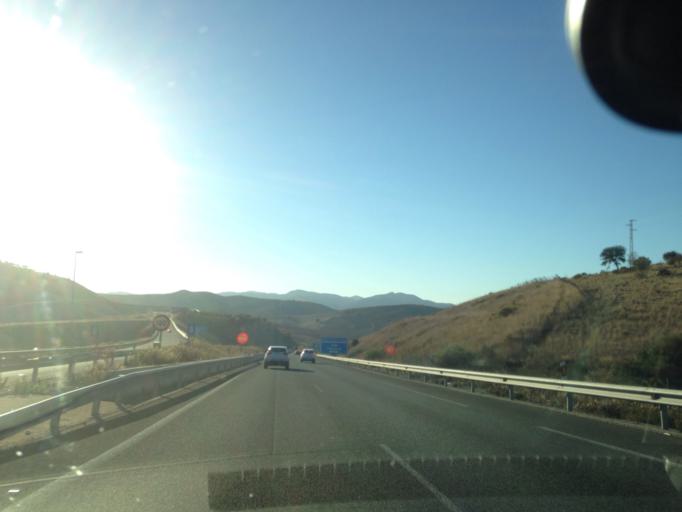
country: ES
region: Andalusia
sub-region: Provincia de Malaga
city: Casabermeja
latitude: 36.9500
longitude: -4.4439
